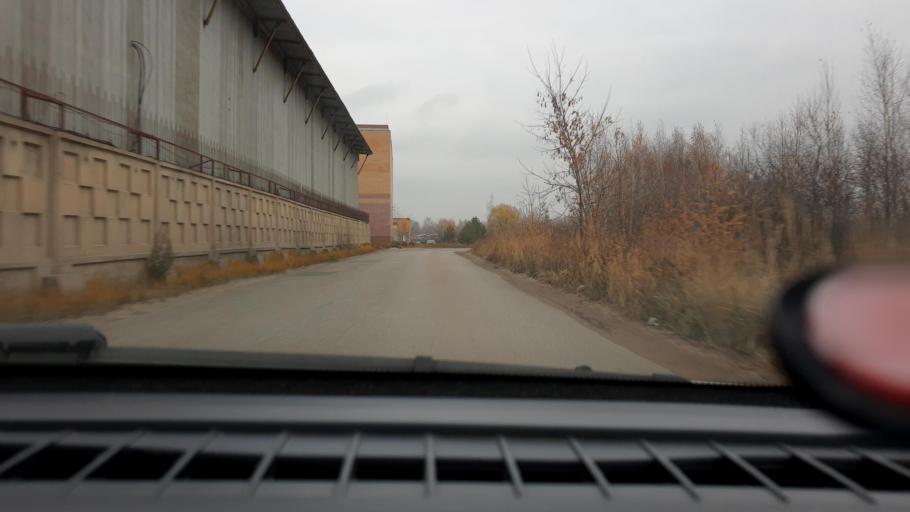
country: RU
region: Nizjnij Novgorod
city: Gorbatovka
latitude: 56.3322
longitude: 43.8100
